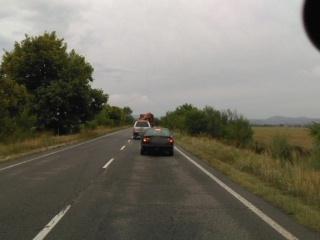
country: BG
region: Plovdiv
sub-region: Obshtina Karlovo
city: Karlovo
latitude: 42.5674
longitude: 24.8282
